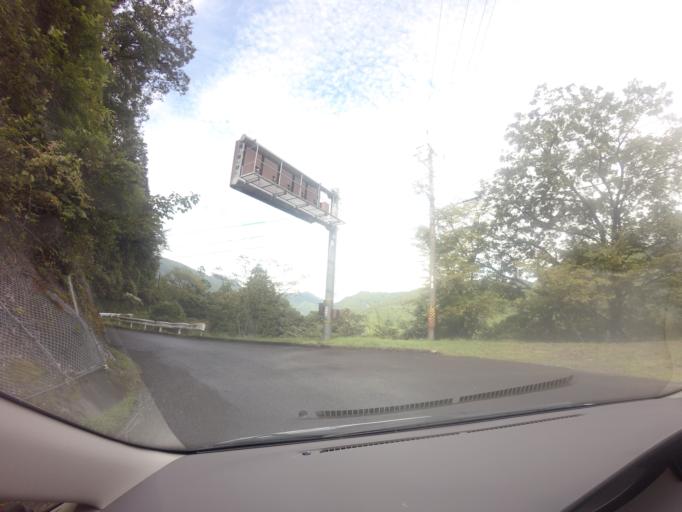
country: JP
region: Wakayama
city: Shingu
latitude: 33.9642
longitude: 135.8508
